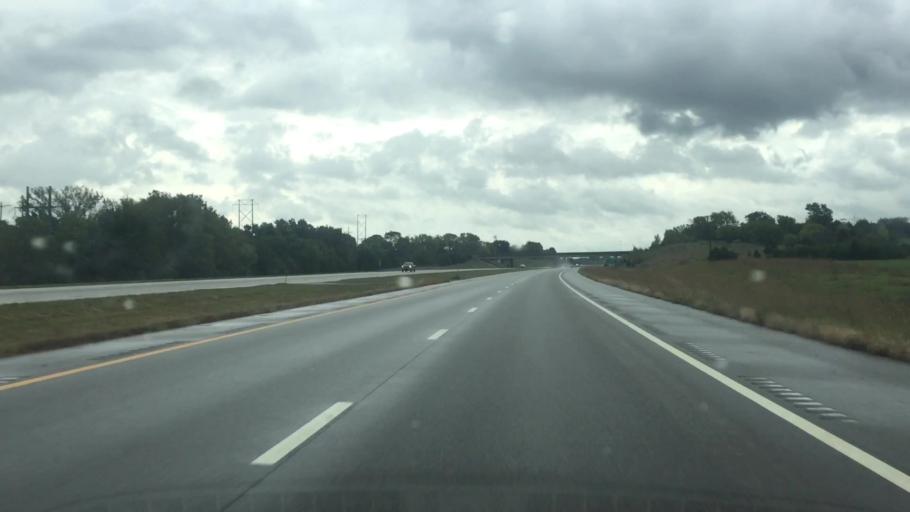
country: US
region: Kansas
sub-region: Miami County
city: Paola
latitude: 38.5597
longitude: -94.8656
